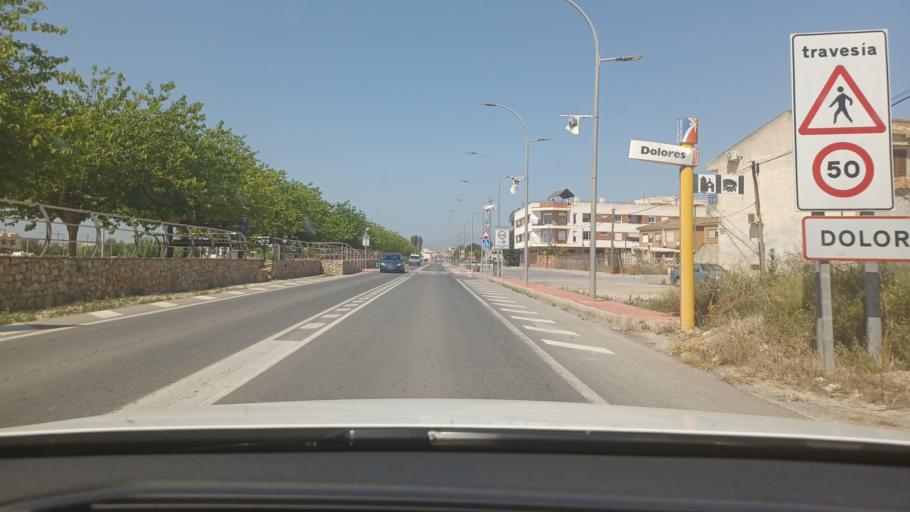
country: ES
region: Valencia
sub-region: Provincia de Alicante
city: Dolores
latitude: 38.1385
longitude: -0.7609
